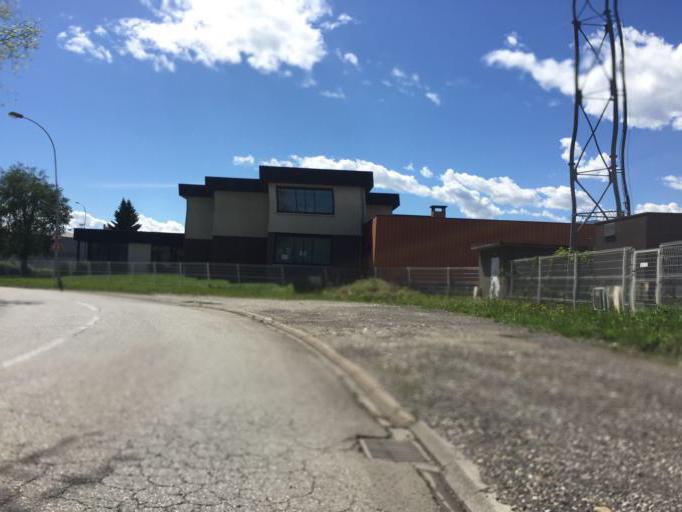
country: FR
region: Rhone-Alpes
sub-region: Departement de la Savoie
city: La Motte-Servolex
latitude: 45.5893
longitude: 5.8960
